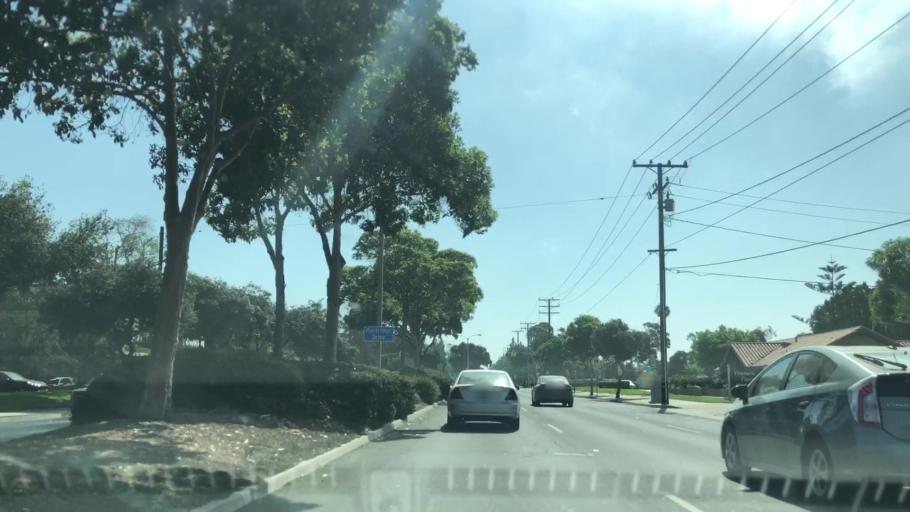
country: US
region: California
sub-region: Ventura County
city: El Rio
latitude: 34.2664
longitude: -119.2050
